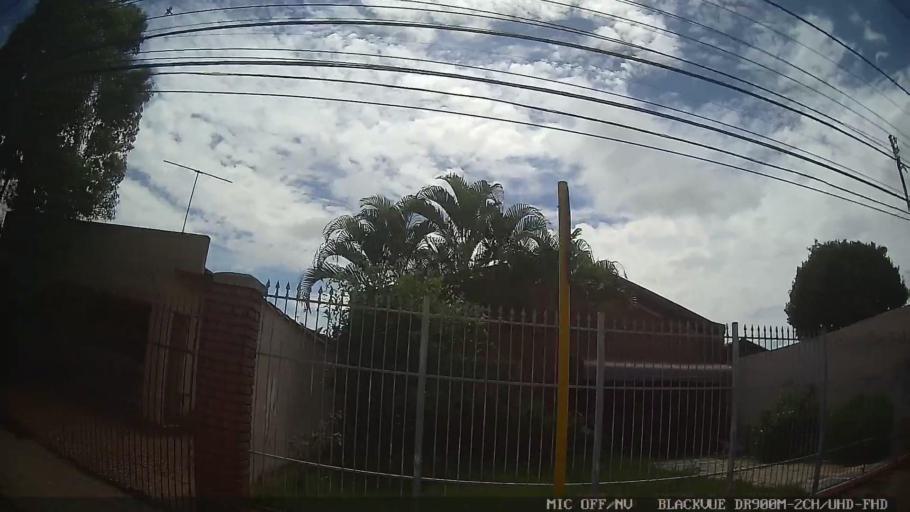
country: BR
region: Sao Paulo
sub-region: Laranjal Paulista
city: Laranjal Paulista
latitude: -23.0561
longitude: -47.8327
